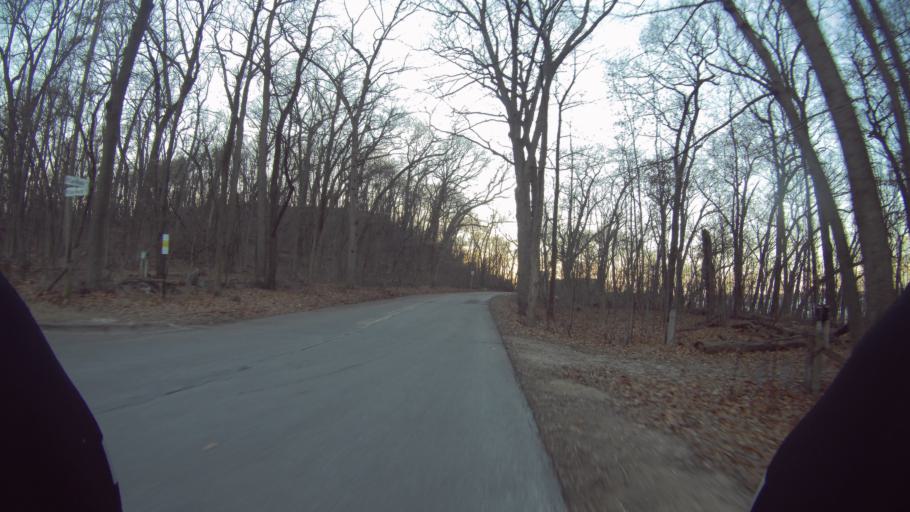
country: US
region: Wisconsin
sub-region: Dane County
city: Shorewood Hills
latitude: 43.0875
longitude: -89.4423
